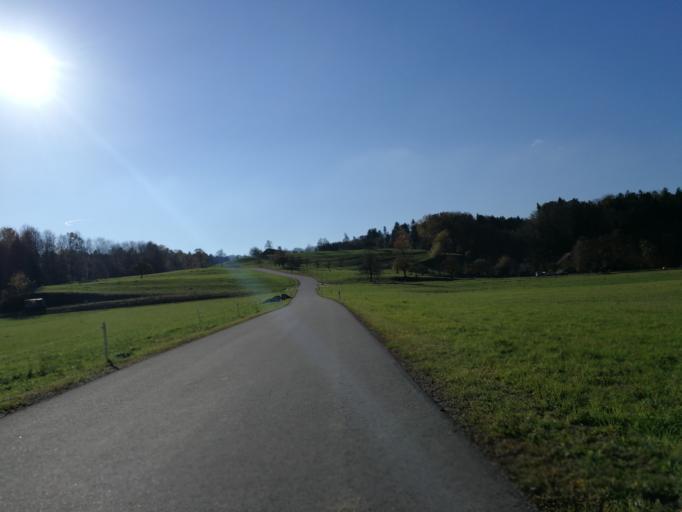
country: CH
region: Zurich
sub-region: Bezirk Uster
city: Monchaltorf
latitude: 47.3077
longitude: 8.7139
